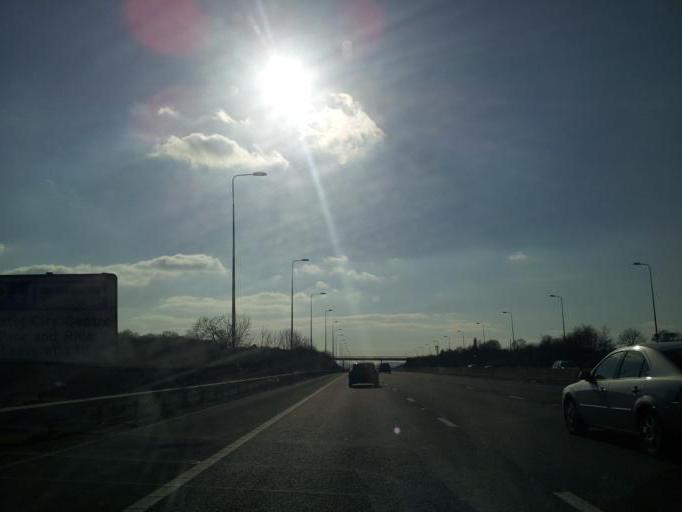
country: GB
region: England
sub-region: South Gloucestershire
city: Severn Beach
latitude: 51.5227
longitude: -2.6269
